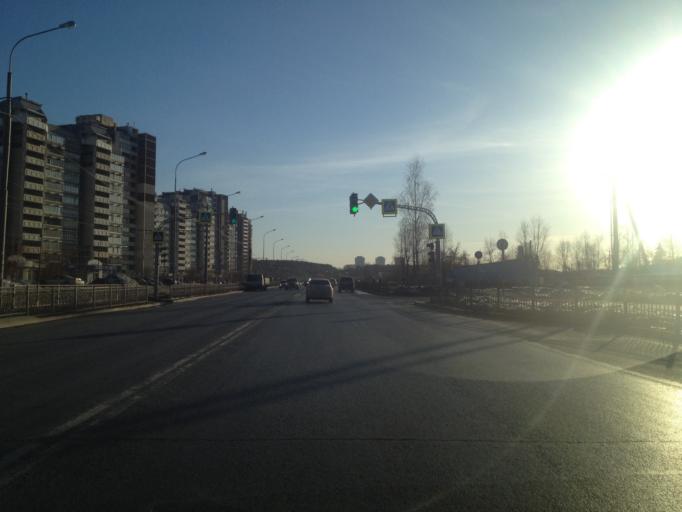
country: RU
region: Sverdlovsk
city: Sovkhoznyy
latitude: 56.8245
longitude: 60.5425
